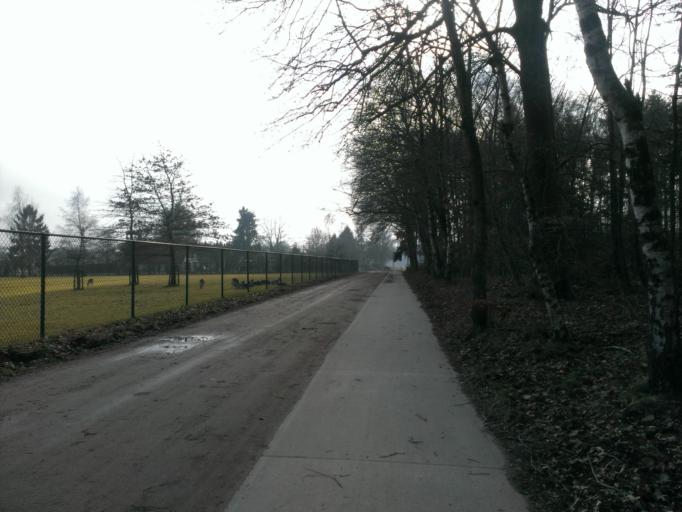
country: NL
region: Gelderland
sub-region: Gemeente Heerde
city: Heerde
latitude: 52.3845
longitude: 6.0085
